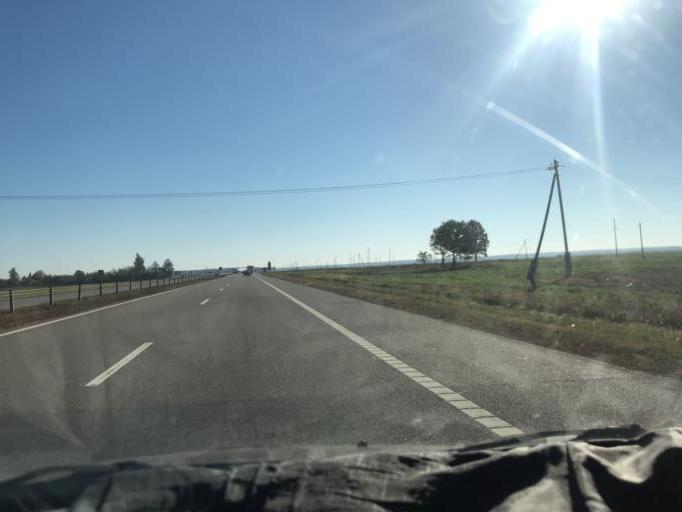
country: BY
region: Mogilev
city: Yalizava
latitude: 53.2362
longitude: 28.9706
